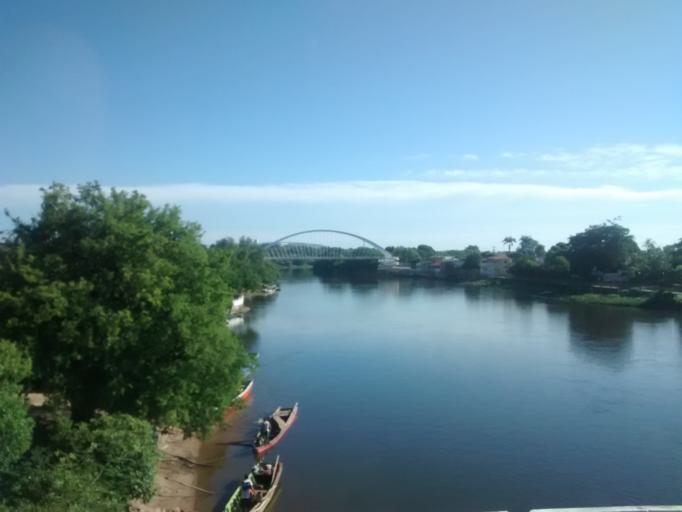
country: BR
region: Bahia
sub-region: Sao Felix Do Coribe
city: Santa Maria da Vitoria
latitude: -13.4010
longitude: -44.1992
